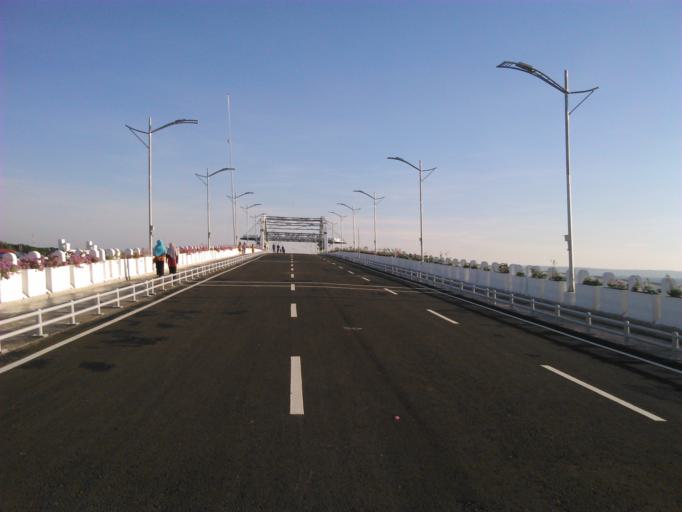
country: ID
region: East Java
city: Labansari
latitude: -7.2394
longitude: 112.7974
